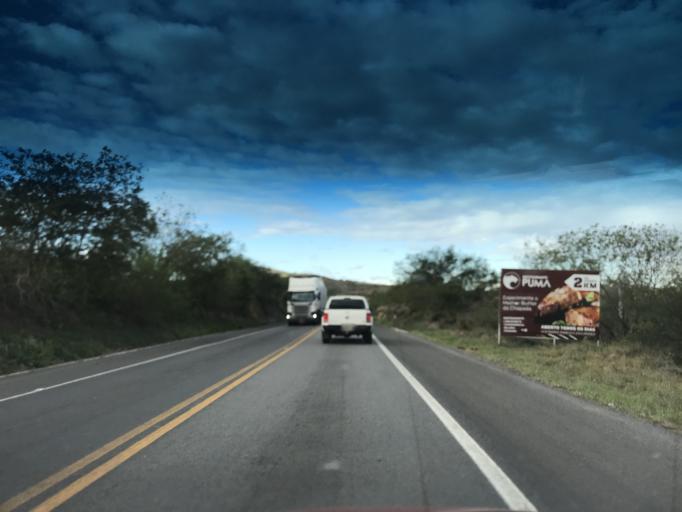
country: BR
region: Bahia
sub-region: Itaberaba
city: Itaberaba
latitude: -12.5172
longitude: -40.3317
